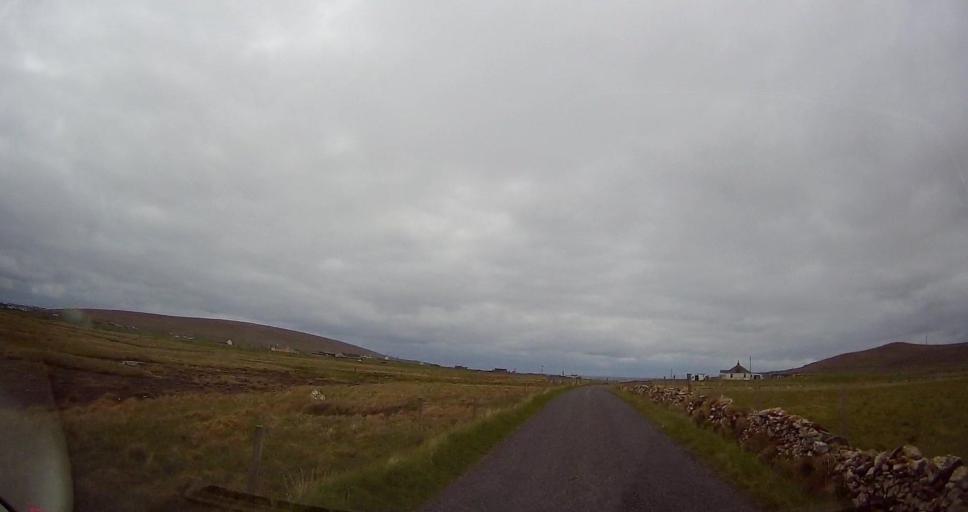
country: GB
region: Scotland
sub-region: Shetland Islands
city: Shetland
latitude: 60.7928
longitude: -0.8499
